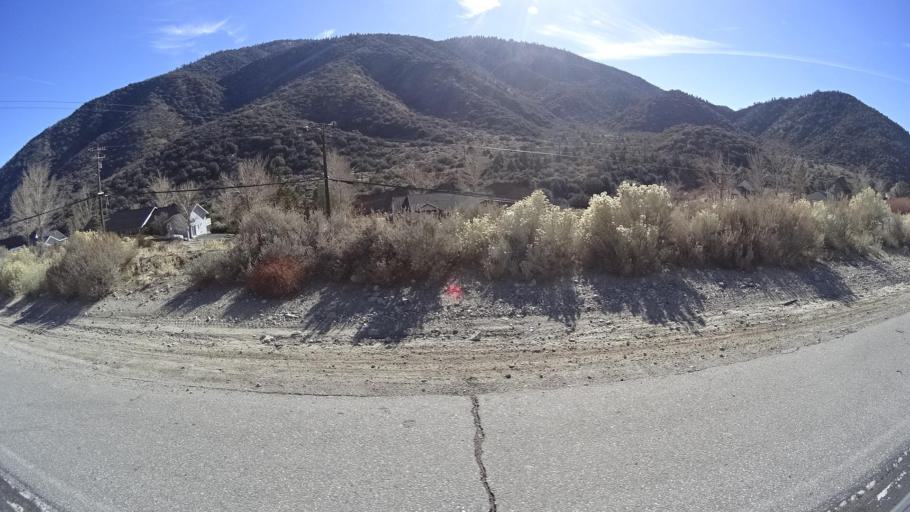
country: US
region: California
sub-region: Kern County
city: Frazier Park
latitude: 34.8212
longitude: -118.9733
